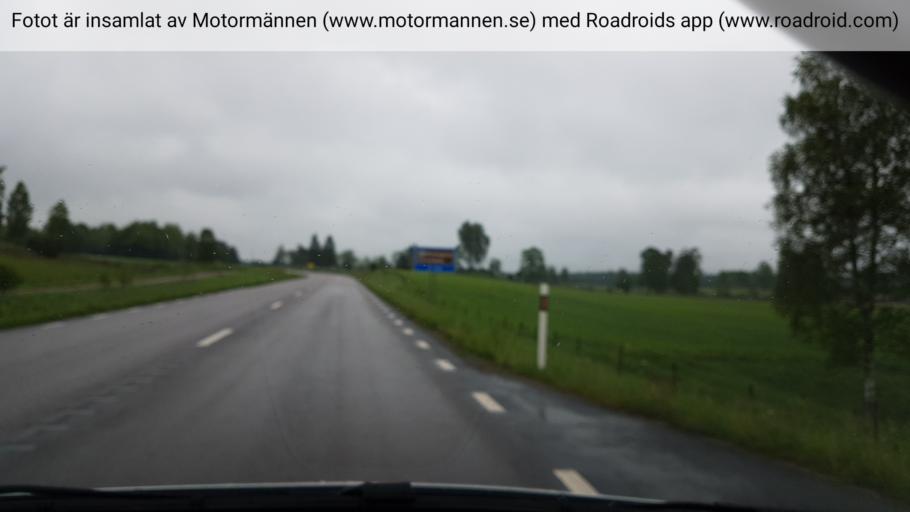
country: SE
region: Vaestra Goetaland
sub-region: Falkopings Kommun
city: Falkoeping
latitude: 58.0091
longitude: 13.5670
